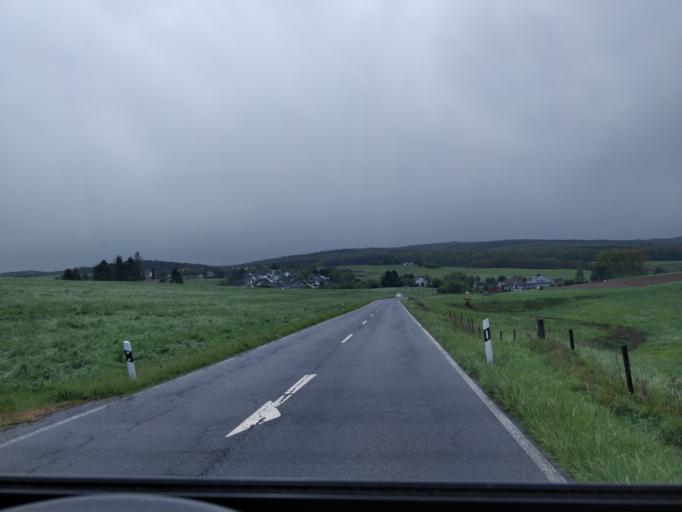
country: DE
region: North Rhine-Westphalia
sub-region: Regierungsbezirk Koln
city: Rheinbach
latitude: 50.6014
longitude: 6.8961
